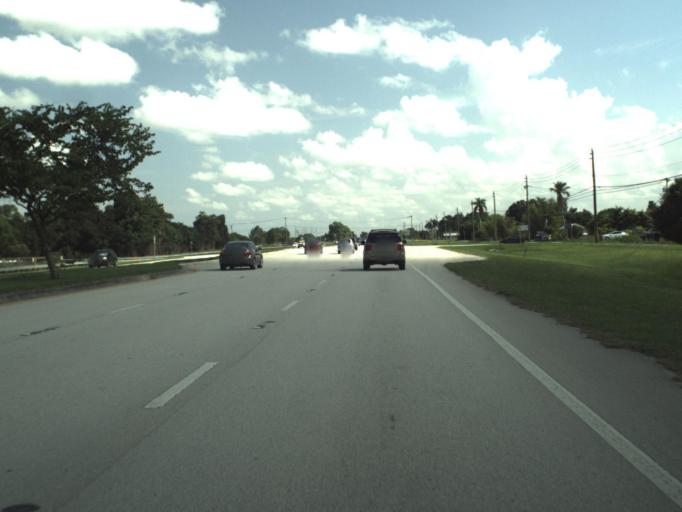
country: US
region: Florida
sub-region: Palm Beach County
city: Greenacres City
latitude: 26.5553
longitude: -80.2059
